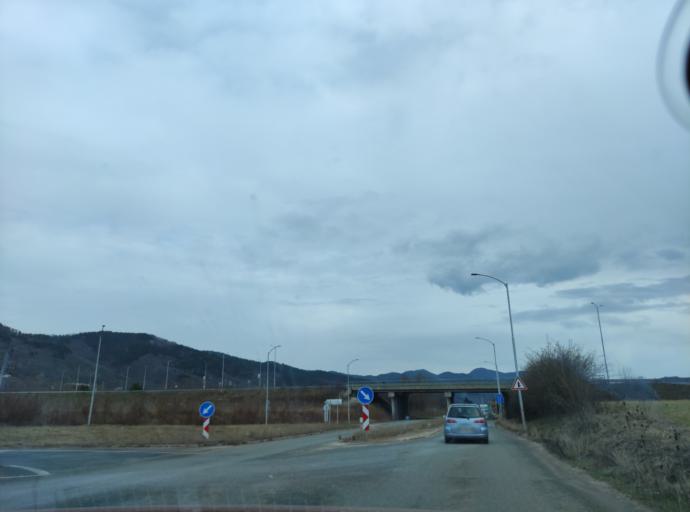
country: BG
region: Sofiya
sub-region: Obshtina Pravets
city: Pravets
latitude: 42.9116
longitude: 23.8880
